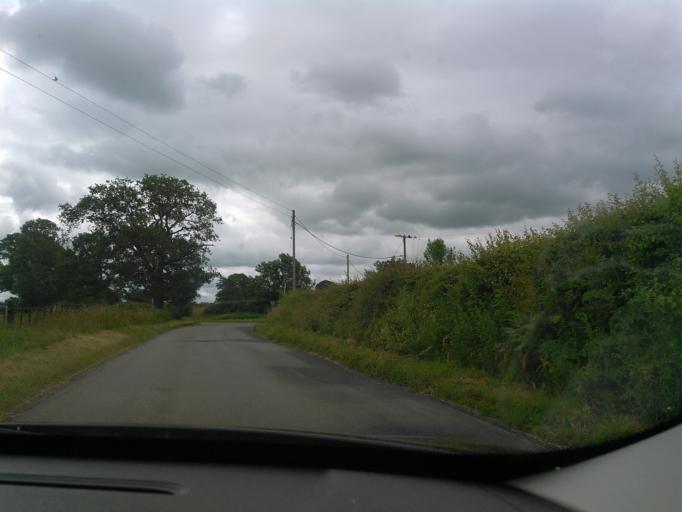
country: GB
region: England
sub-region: Shropshire
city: Wem
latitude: 52.9115
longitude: -2.7314
